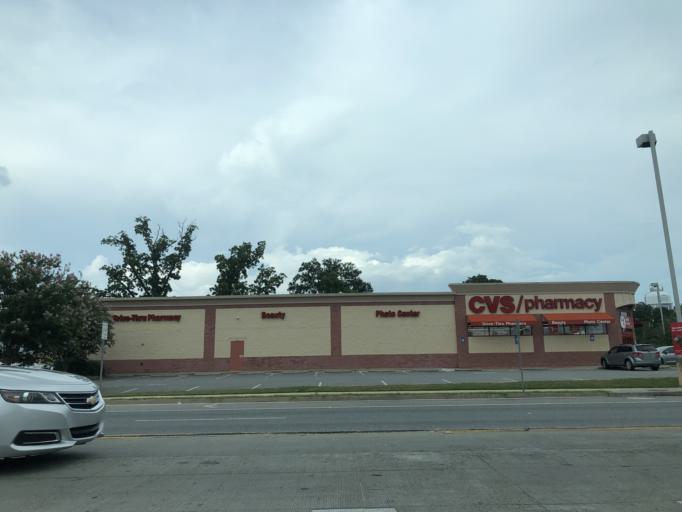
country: US
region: Georgia
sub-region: Wayne County
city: Jesup
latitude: 31.6096
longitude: -81.8836
